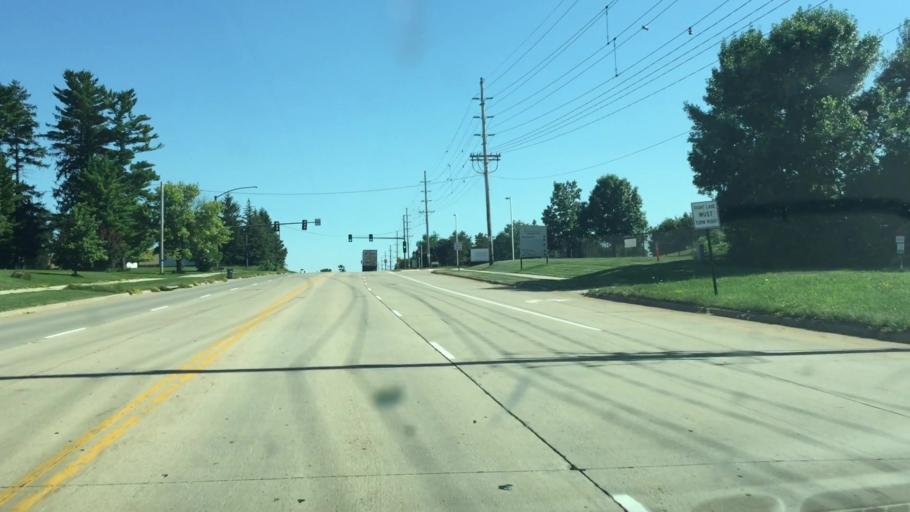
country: US
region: Iowa
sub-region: Linn County
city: Ely
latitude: 41.9195
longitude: -91.6373
